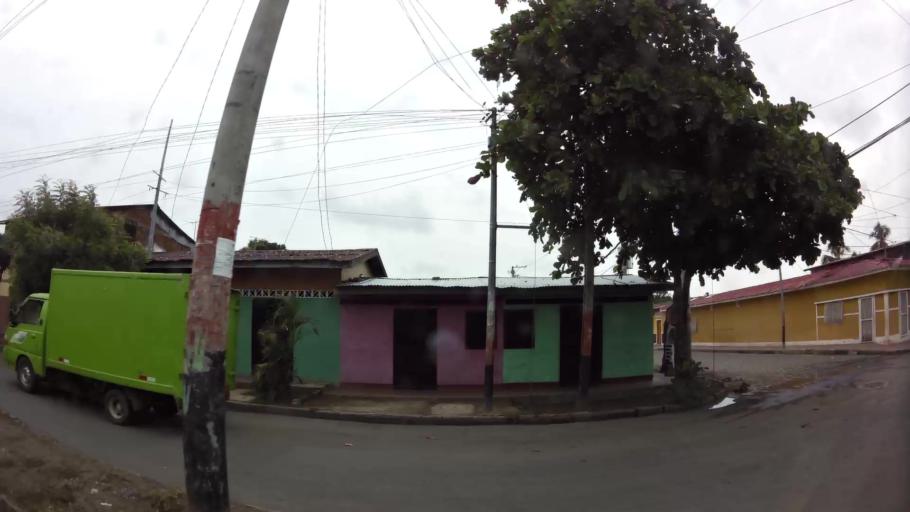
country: NI
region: Granada
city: Granada
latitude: 11.9282
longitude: -85.9461
